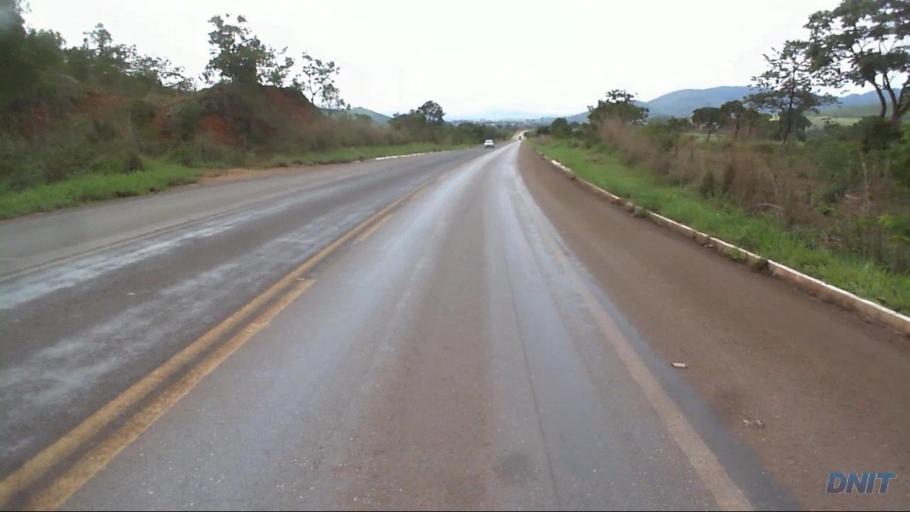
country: BR
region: Goias
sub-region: Barro Alto
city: Barro Alto
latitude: -14.9403
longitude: -48.9391
